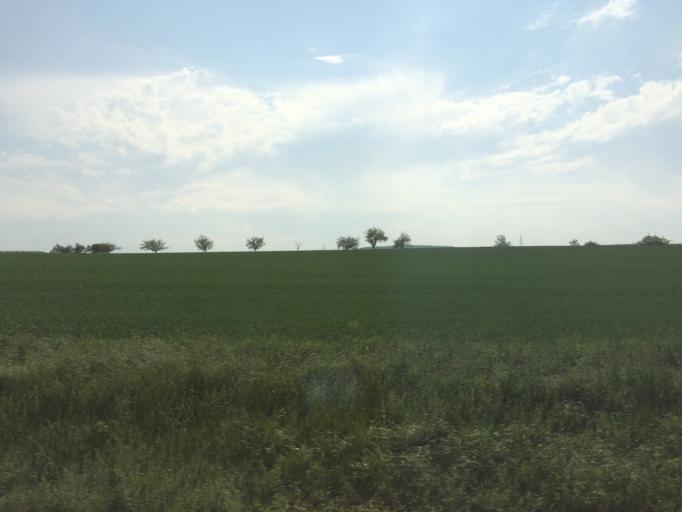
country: DE
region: Bavaria
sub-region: Regierungsbezirk Mittelfranken
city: Langenfeld
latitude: 49.6064
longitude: 10.5326
